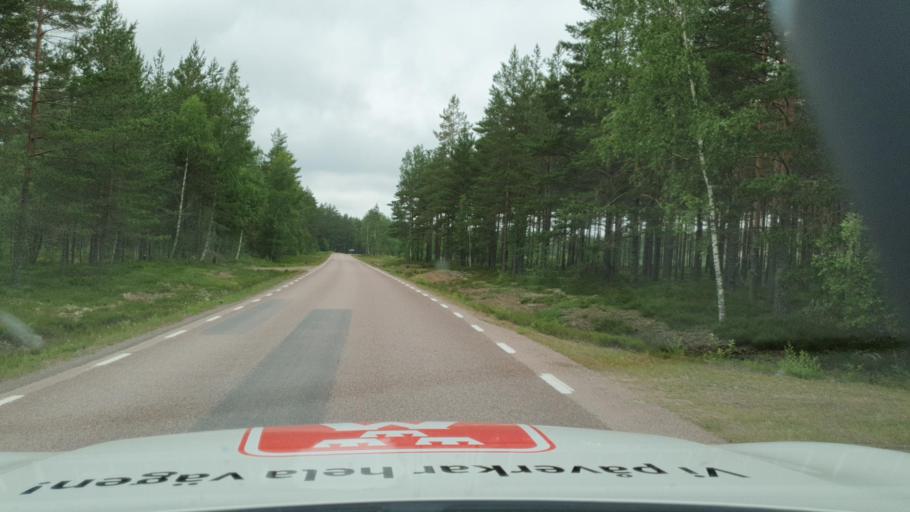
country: SE
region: Vaermland
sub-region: Kristinehamns Kommun
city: Kristinehamn
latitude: 59.5129
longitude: 13.9513
